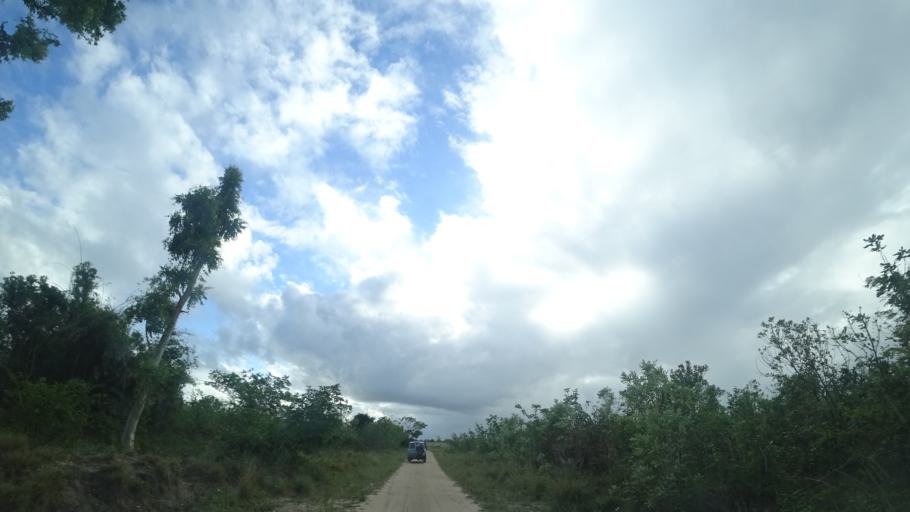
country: MZ
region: Sofala
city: Beira
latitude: -19.6653
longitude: 35.0592
